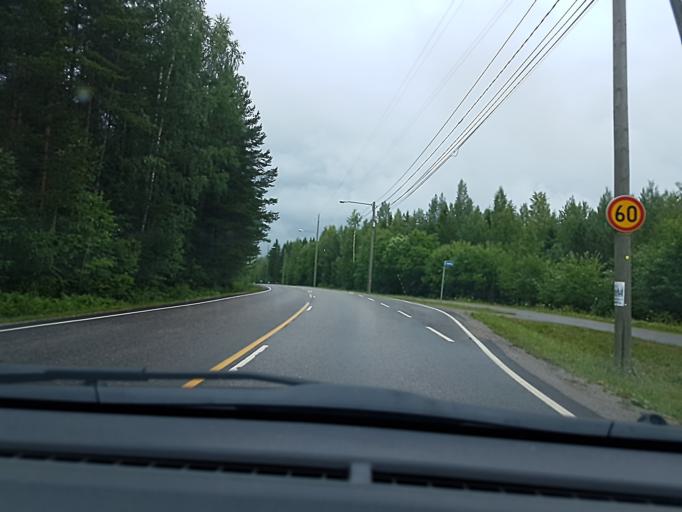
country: FI
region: Uusimaa
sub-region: Helsinki
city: Pornainen
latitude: 60.4648
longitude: 25.3903
